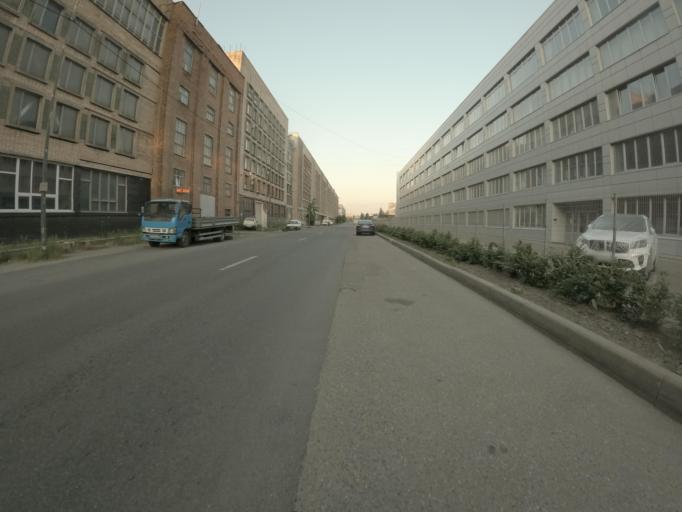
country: RU
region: St.-Petersburg
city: Admiralteisky
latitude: 59.8878
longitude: 30.2826
